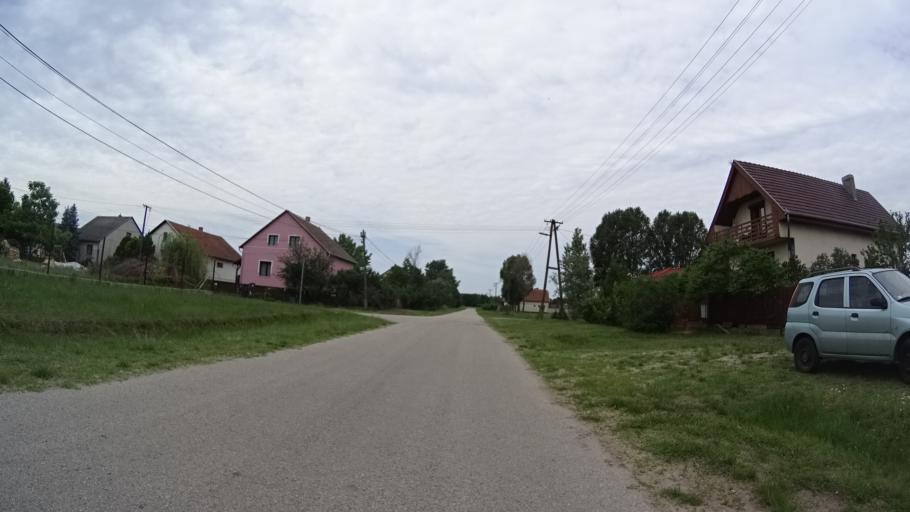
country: HU
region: Bacs-Kiskun
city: Tiszakecske
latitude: 46.9228
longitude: 20.0695
